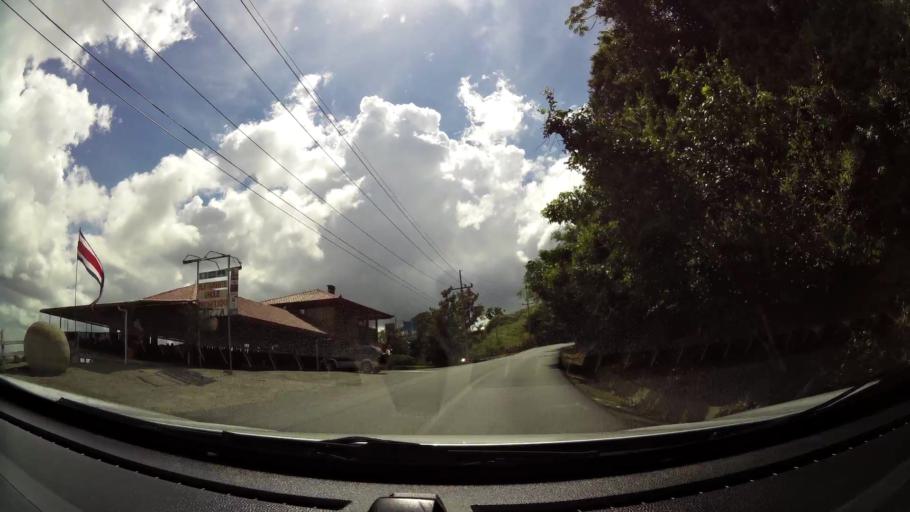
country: CR
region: San Jose
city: San Isidro
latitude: 9.3330
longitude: -83.7333
